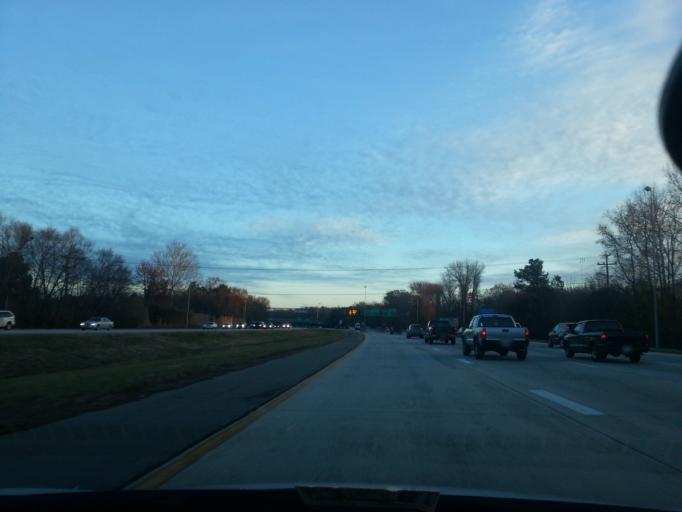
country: US
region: Virginia
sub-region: City of Chesapeake
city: Chesapeake
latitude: 36.8022
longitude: -76.1989
